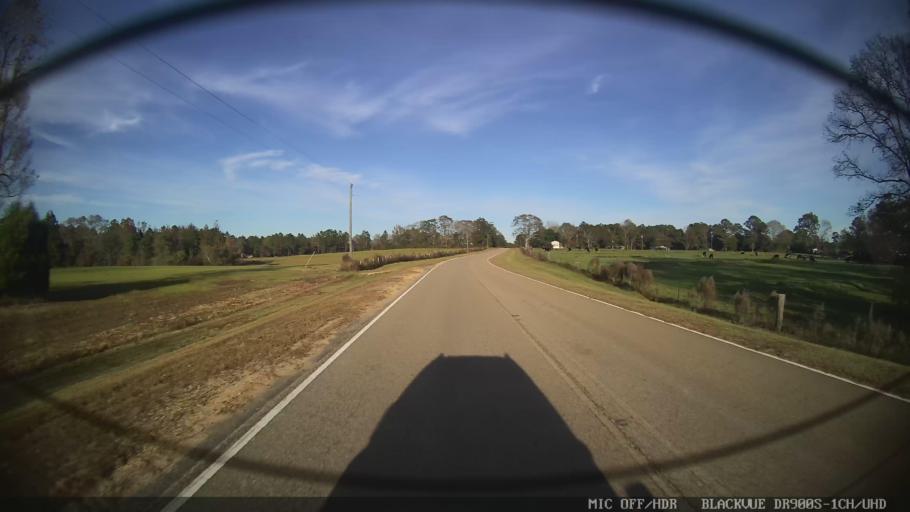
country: US
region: Mississippi
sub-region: Lamar County
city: Purvis
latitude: 31.1683
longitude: -89.3037
